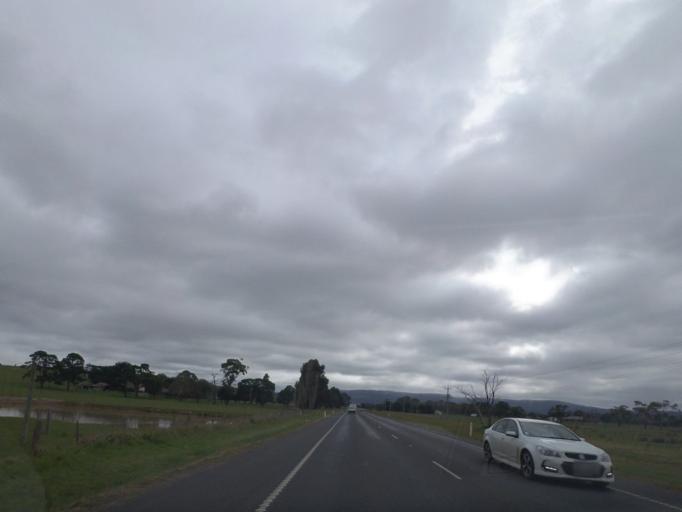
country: AU
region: Victoria
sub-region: Whittlesea
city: Whittlesea
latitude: -37.5411
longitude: 145.1103
